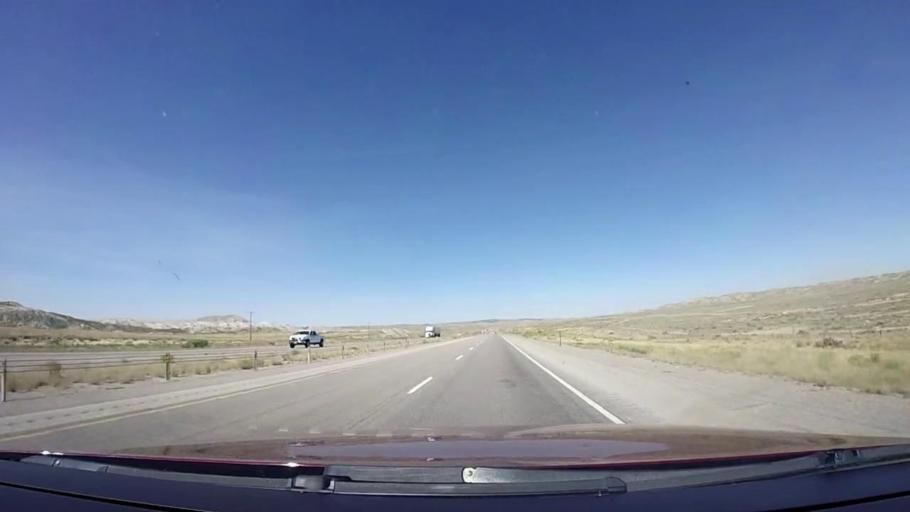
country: US
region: Wyoming
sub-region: Sweetwater County
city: Rock Springs
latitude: 41.6470
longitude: -108.6586
